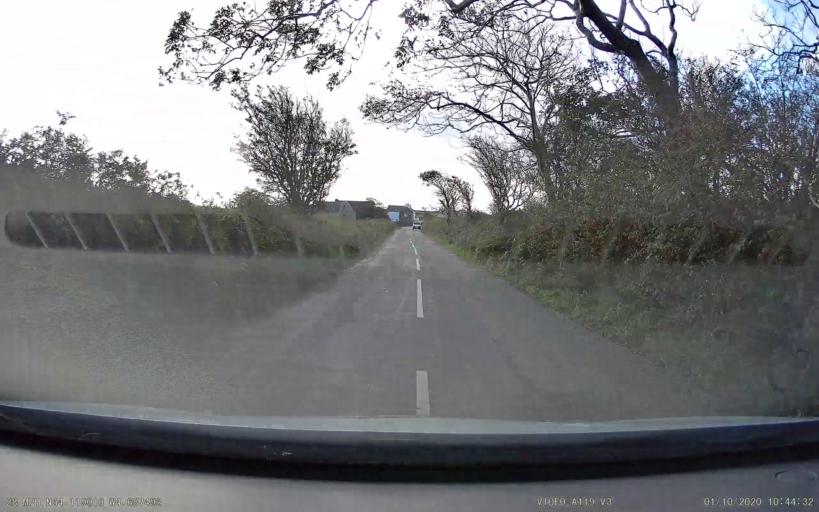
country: IM
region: Castletown
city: Castletown
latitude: 54.1190
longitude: -4.6875
